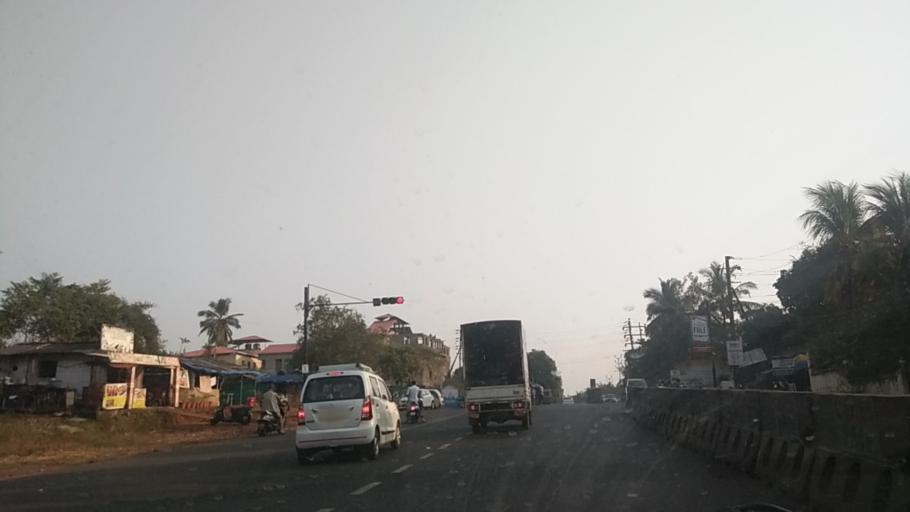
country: IN
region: Goa
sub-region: North Goa
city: Serula
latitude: 15.5423
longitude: 73.8213
